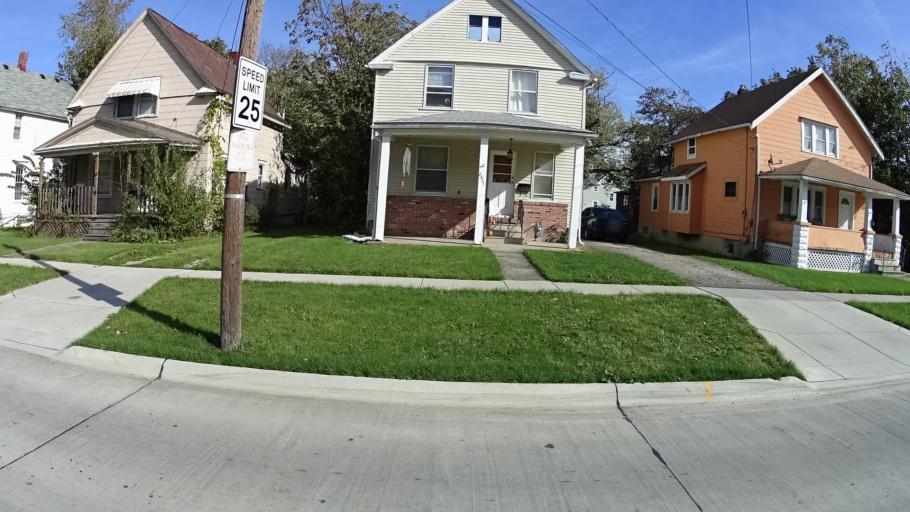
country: US
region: Ohio
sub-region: Lorain County
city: Lorain
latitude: 41.4481
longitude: -82.1683
